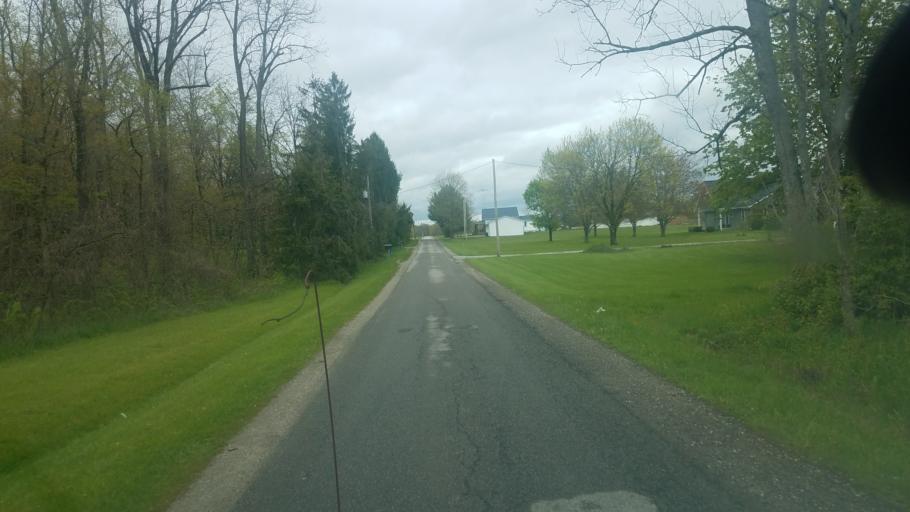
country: US
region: Ohio
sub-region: Crawford County
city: Bucyrus
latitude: 40.7514
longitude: -83.0736
